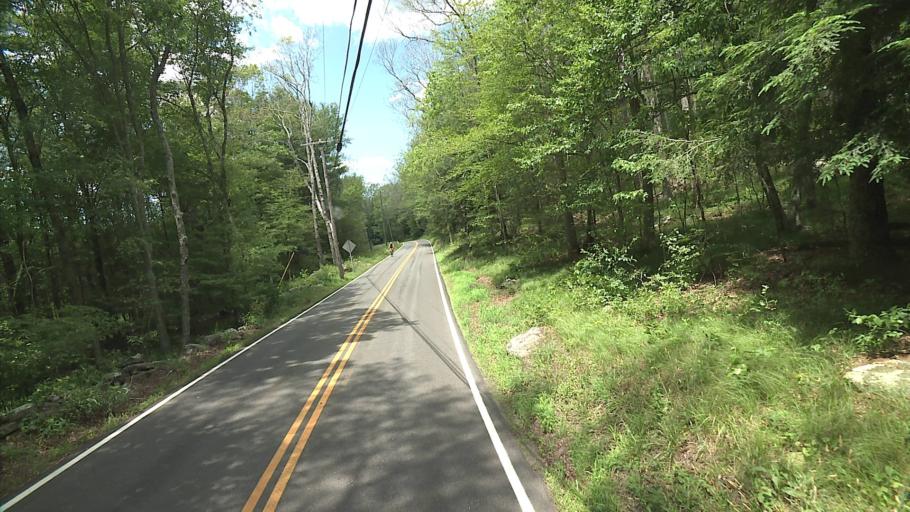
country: US
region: Connecticut
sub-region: New London County
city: Colchester
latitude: 41.4882
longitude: -72.3440
